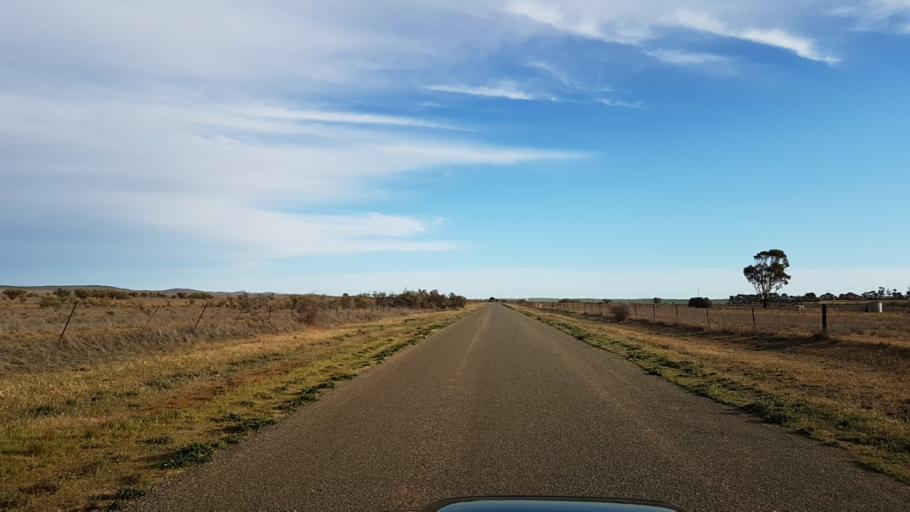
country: AU
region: South Australia
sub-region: Peterborough
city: Peterborough
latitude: -32.9862
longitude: 138.8503
